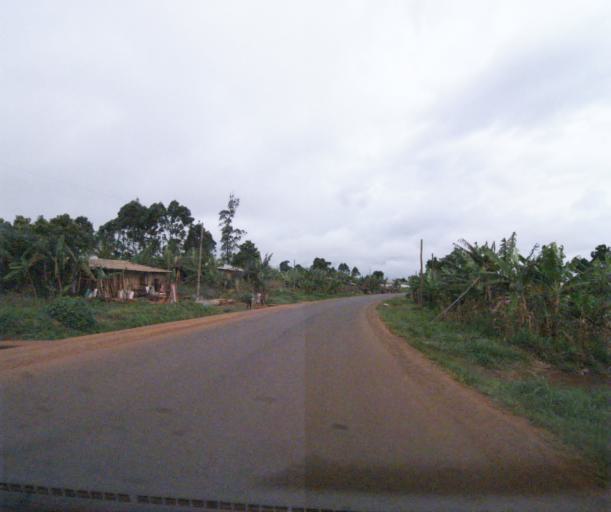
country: CM
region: West
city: Dschang
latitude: 5.4963
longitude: 10.1576
